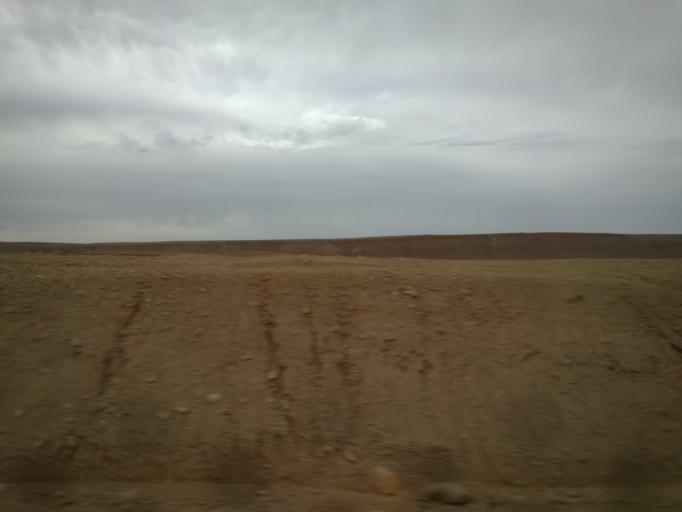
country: IL
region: Southern District
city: Eilat
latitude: 29.8498
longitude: 34.8404
